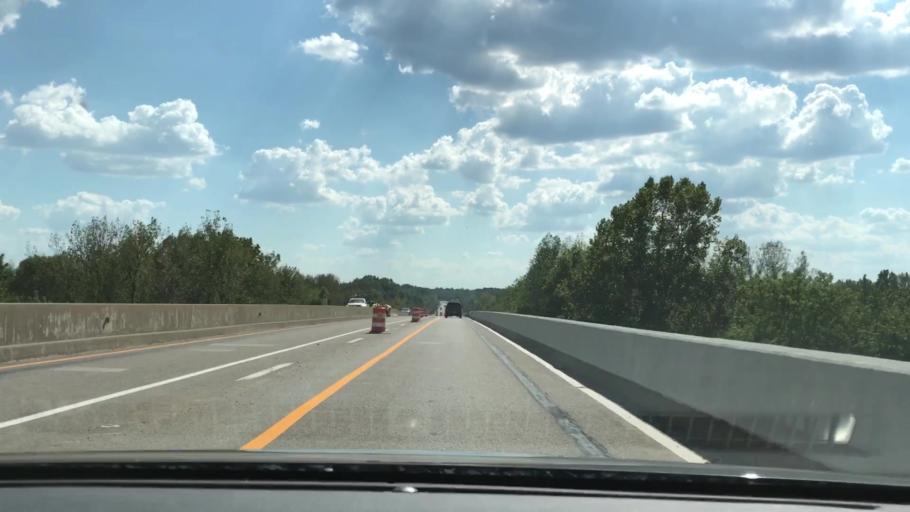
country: US
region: Kentucky
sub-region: Ohio County
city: Oak Grove
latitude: 37.2822
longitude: -86.7437
